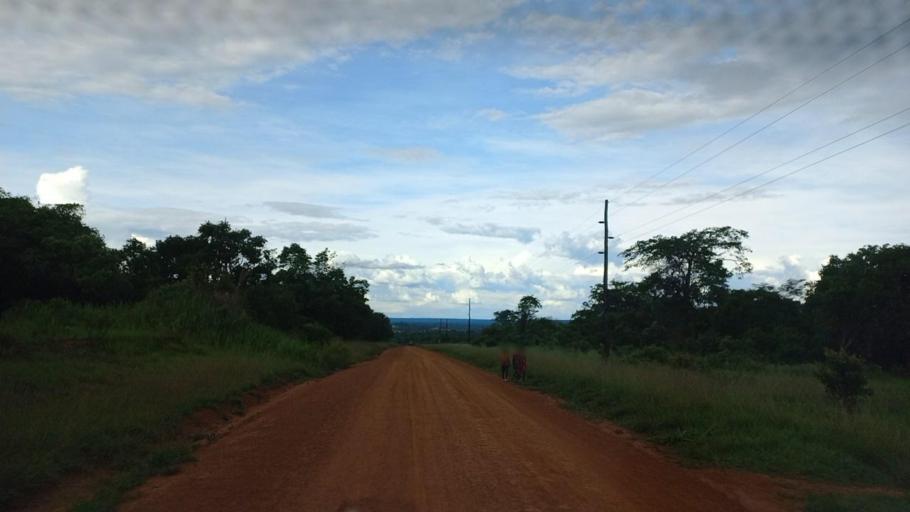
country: ZM
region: North-Western
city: Mwinilunga
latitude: -11.7650
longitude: 24.4128
